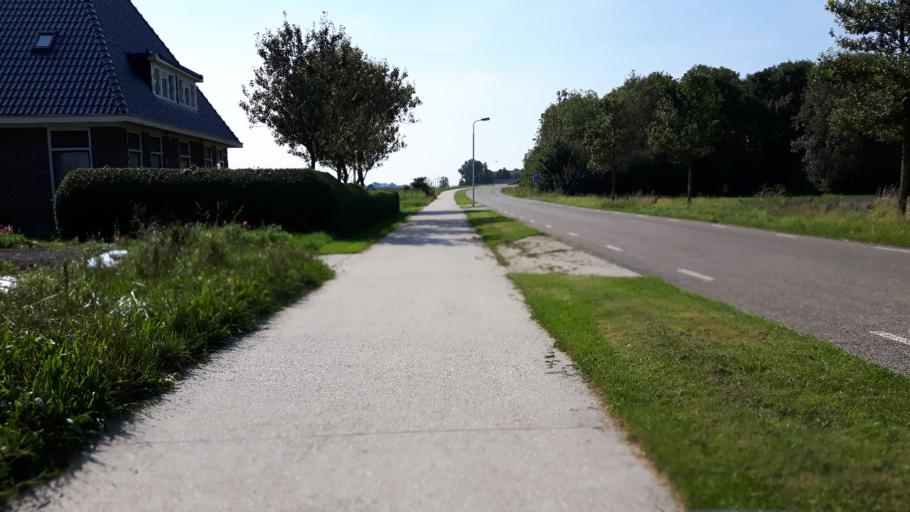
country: NL
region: Friesland
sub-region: Gemeente Franekeradeel
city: Franeker
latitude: 53.2095
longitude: 5.5557
